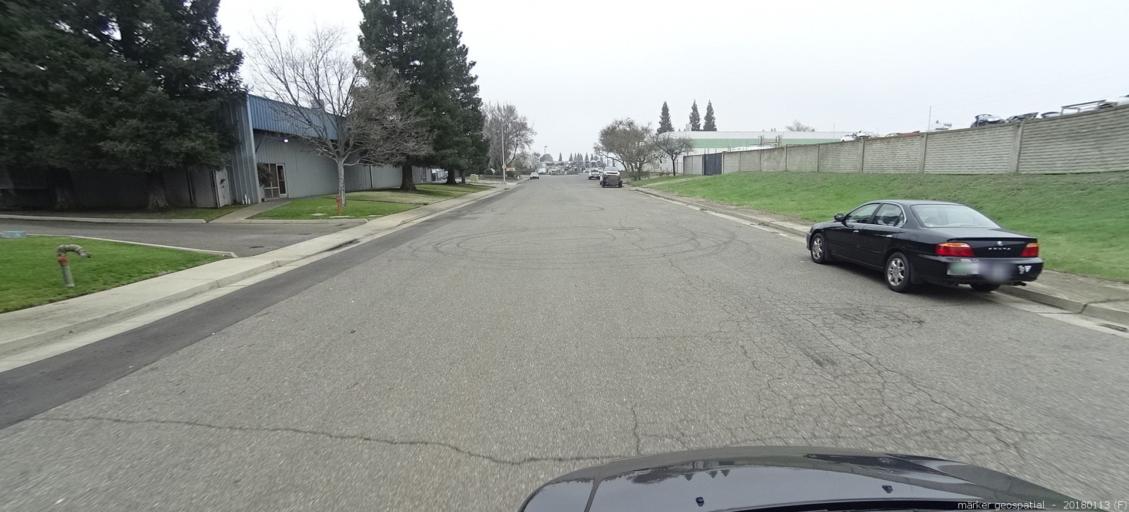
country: US
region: California
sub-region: Sacramento County
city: Rancho Cordova
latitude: 38.5659
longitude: -121.2548
